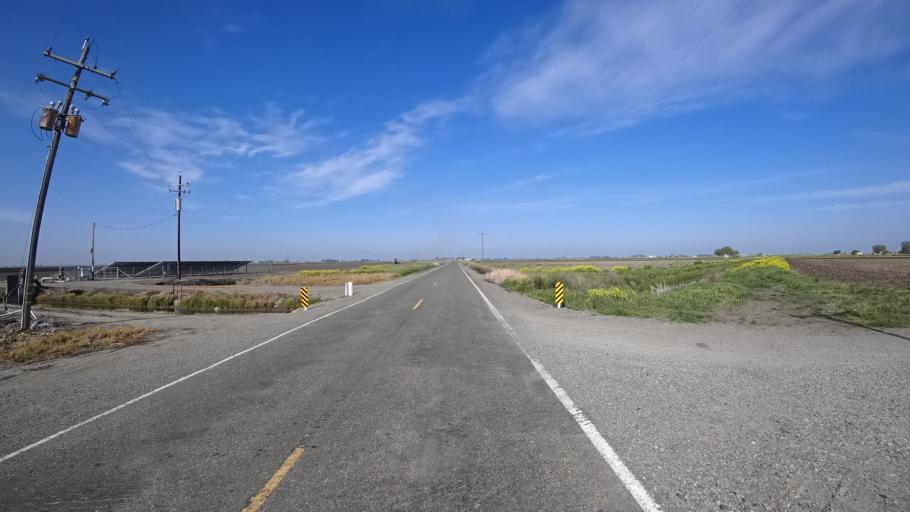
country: US
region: California
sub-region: Glenn County
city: Willows
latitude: 39.5581
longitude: -122.0603
